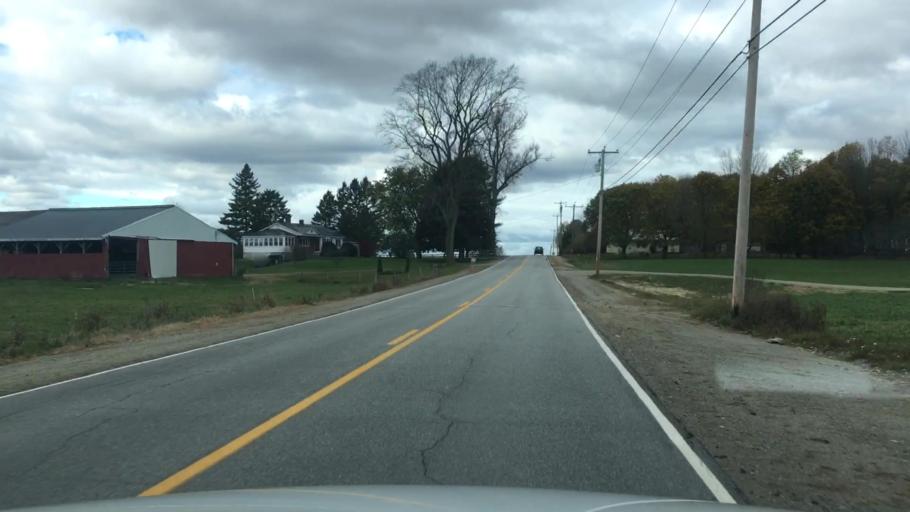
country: US
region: Maine
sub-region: Kennebec County
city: Monmouth
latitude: 44.1974
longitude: -70.0726
